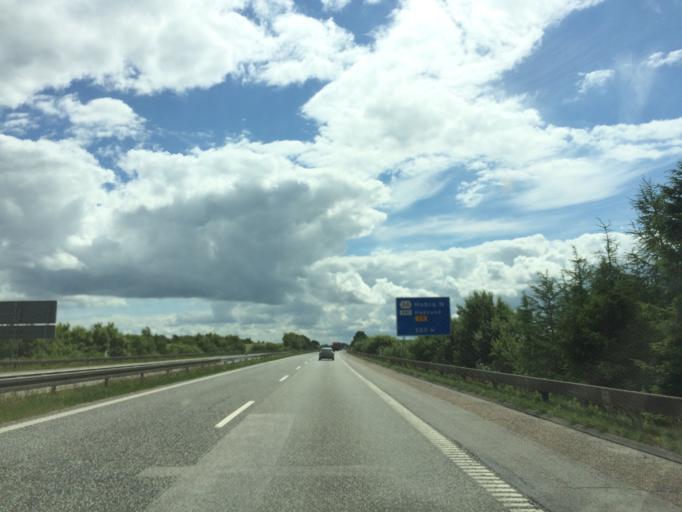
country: DK
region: North Denmark
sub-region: Mariagerfjord Kommune
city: Hobro
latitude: 56.6776
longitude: 9.7329
